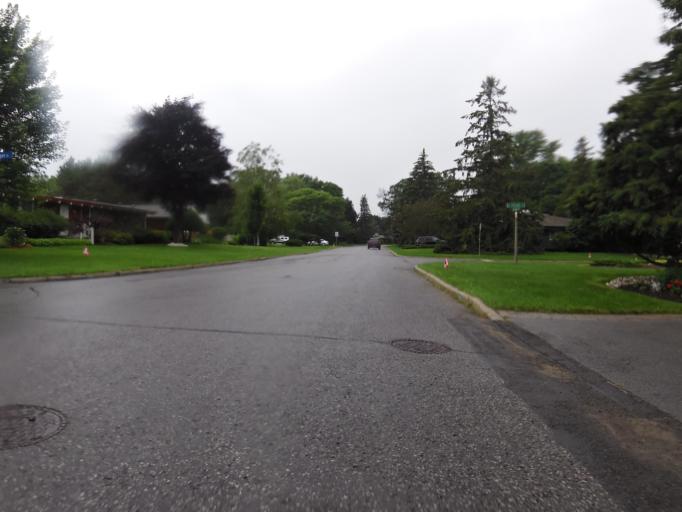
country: CA
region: Ontario
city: Bells Corners
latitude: 45.3420
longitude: -75.8027
